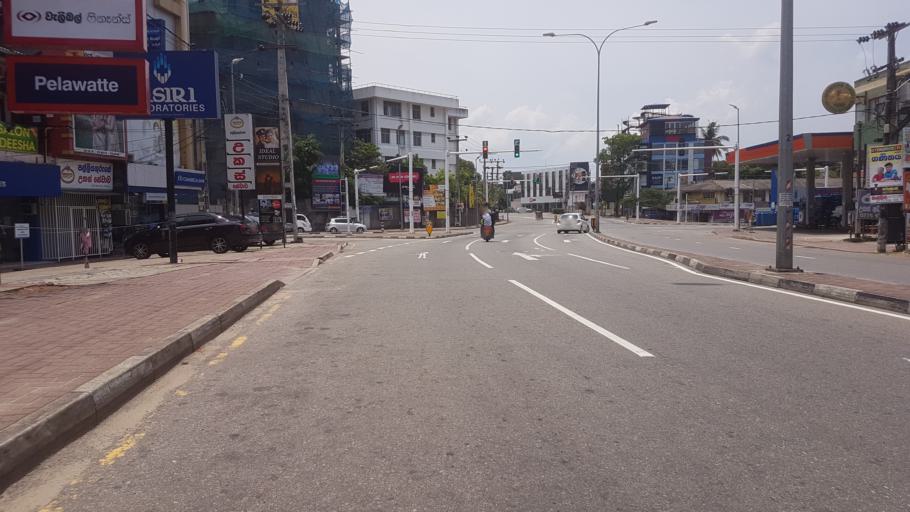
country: LK
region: Western
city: Battaramulla South
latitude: 6.8920
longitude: 79.9288
